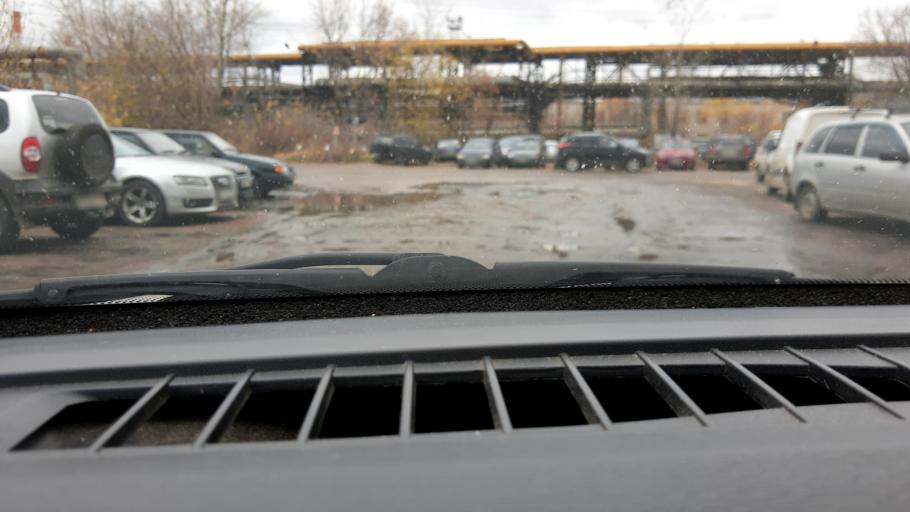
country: RU
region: Nizjnij Novgorod
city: Nizhniy Novgorod
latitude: 56.2418
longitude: 43.9052
